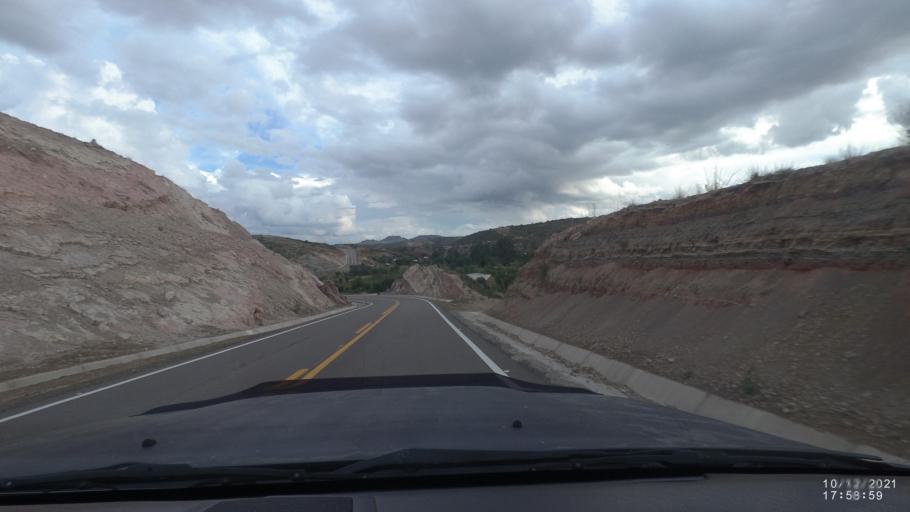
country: BO
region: Cochabamba
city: Cliza
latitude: -17.7303
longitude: -65.9278
